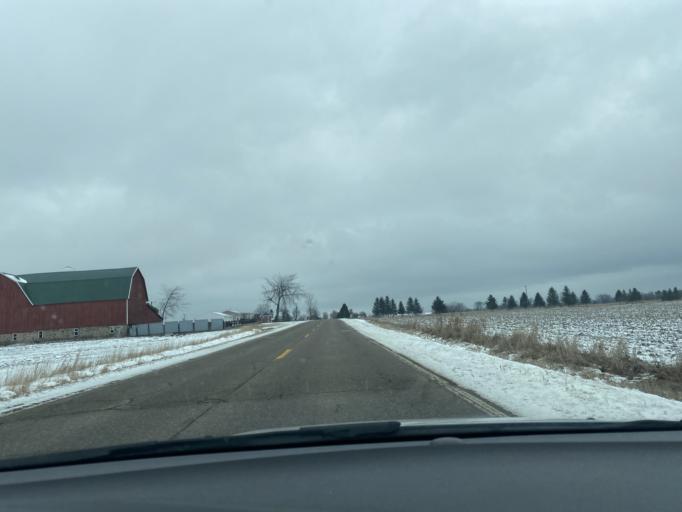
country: US
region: Michigan
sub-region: Lapeer County
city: North Branch
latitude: 43.2101
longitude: -83.1004
